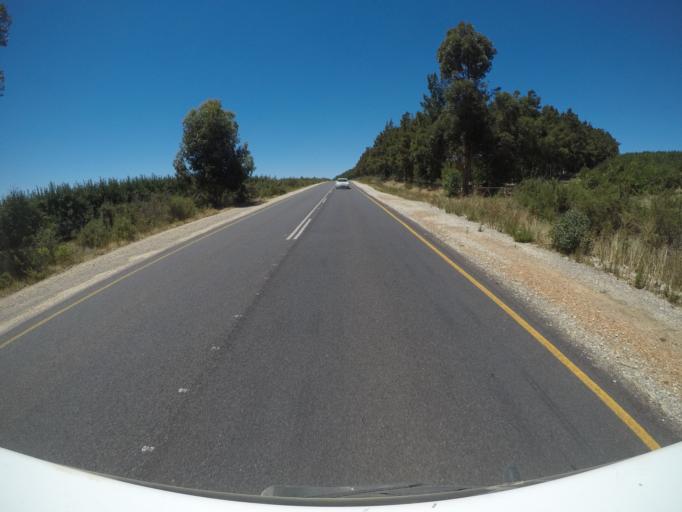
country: ZA
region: Western Cape
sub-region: Overberg District Municipality
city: Grabouw
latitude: -34.0678
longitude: 19.1262
